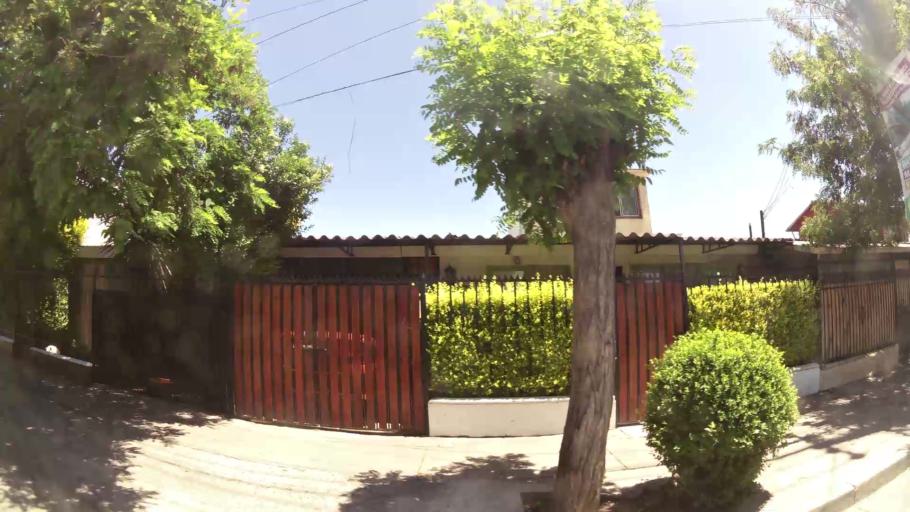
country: CL
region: Santiago Metropolitan
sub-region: Provincia de Santiago
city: La Pintana
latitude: -33.5751
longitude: -70.6668
